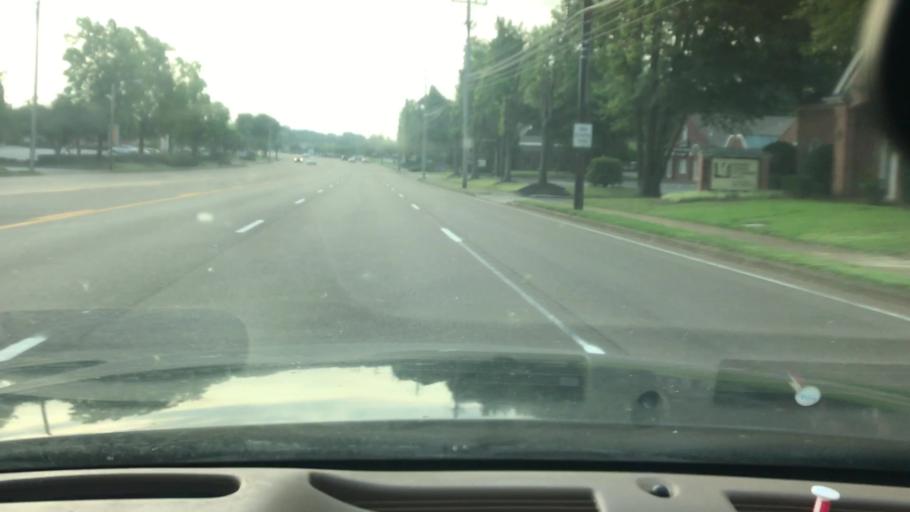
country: US
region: Tennessee
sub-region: Shelby County
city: Bartlett
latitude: 35.2047
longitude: -89.8442
